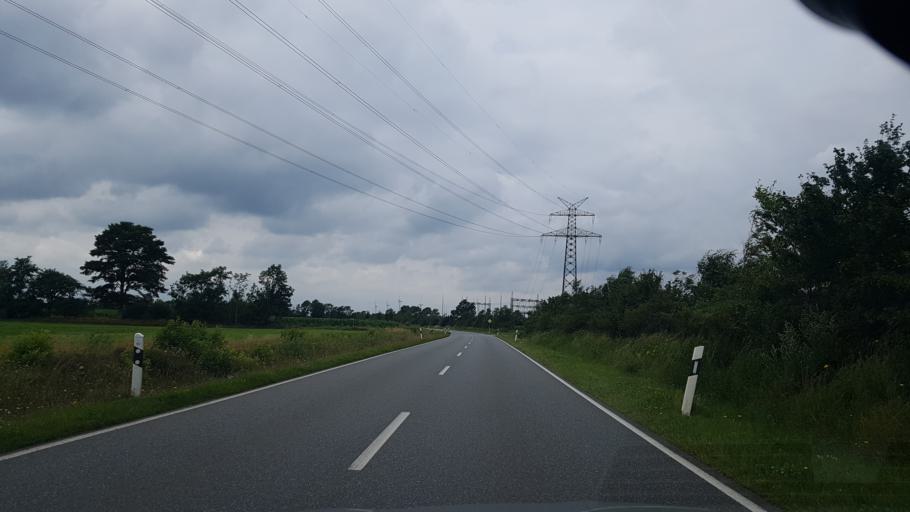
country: DE
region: Schleswig-Holstein
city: Jardelund
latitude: 54.8467
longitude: 9.2019
